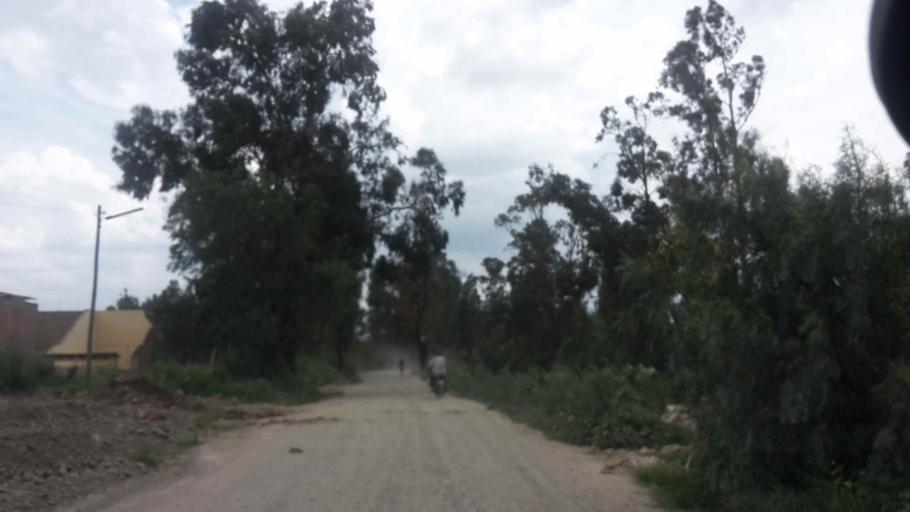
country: BO
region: Cochabamba
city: Cochabamba
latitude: -17.3329
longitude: -66.2241
